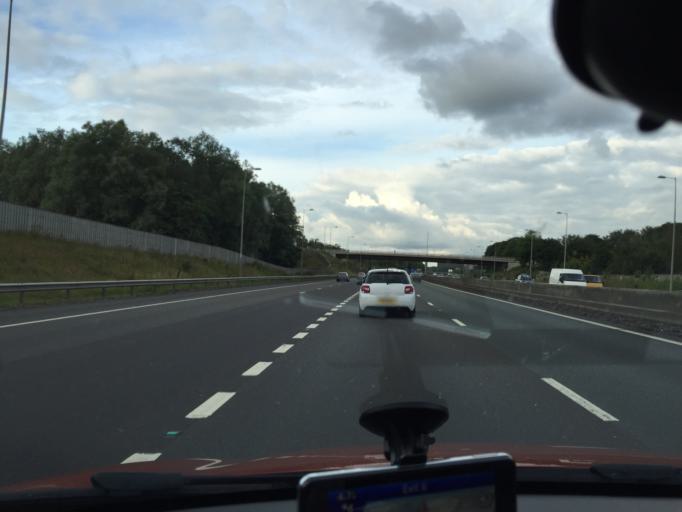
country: GB
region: Scotland
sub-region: North Lanarkshire
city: Cumbernauld
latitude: 55.9356
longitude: -4.0316
